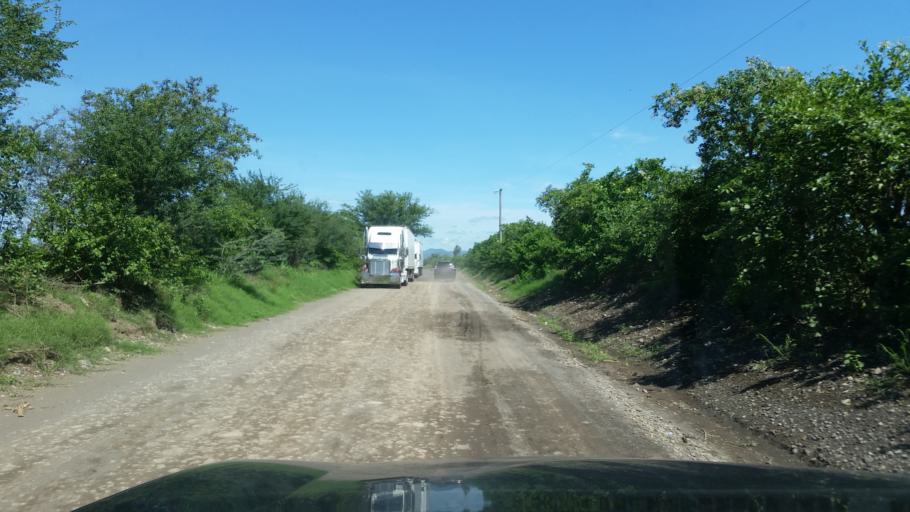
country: NI
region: Chinandega
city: Puerto Morazan
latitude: 12.7715
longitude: -87.0903
